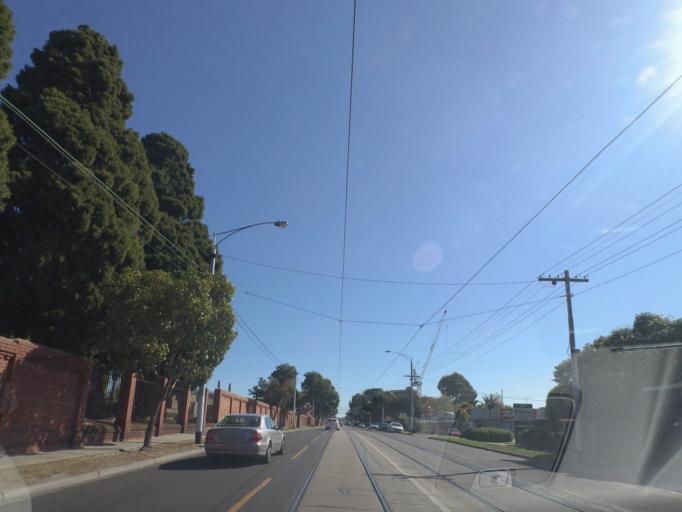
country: AU
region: Victoria
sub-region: Boroondara
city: Kew
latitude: -37.8029
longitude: 145.0418
